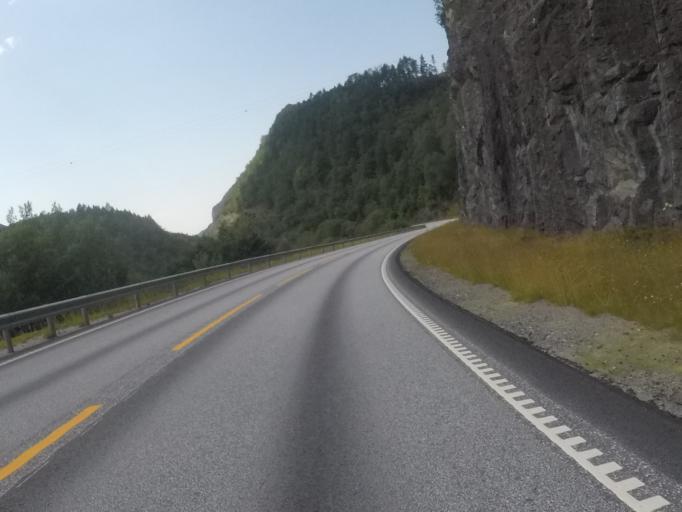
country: NO
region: Sogn og Fjordane
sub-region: Bremanger
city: Svelgen
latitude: 61.6116
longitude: 5.3192
